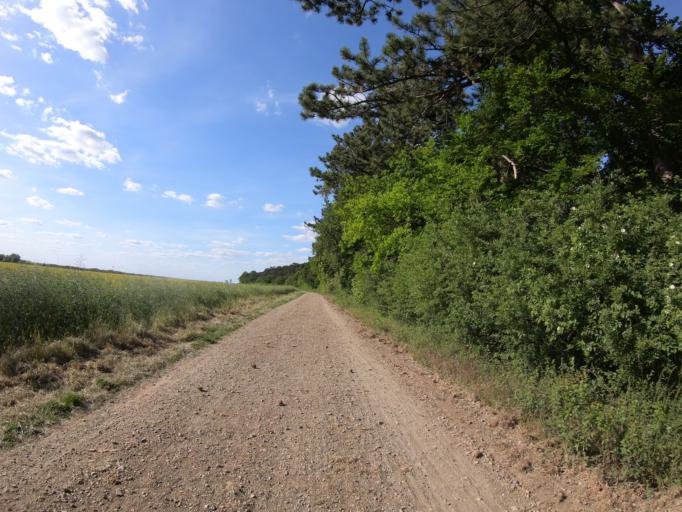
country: DE
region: Lower Saxony
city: Wolfenbuettel
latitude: 52.1872
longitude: 10.5286
